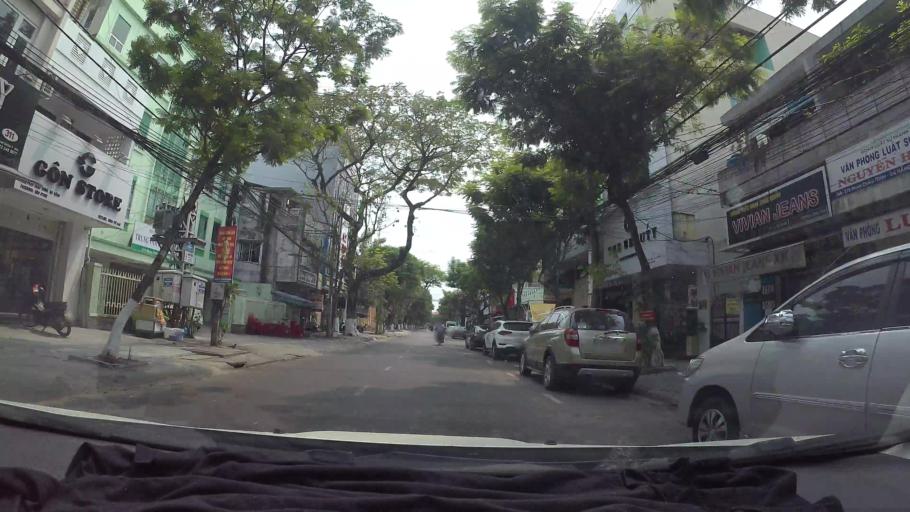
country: VN
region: Da Nang
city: Da Nang
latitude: 16.0589
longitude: 108.2192
